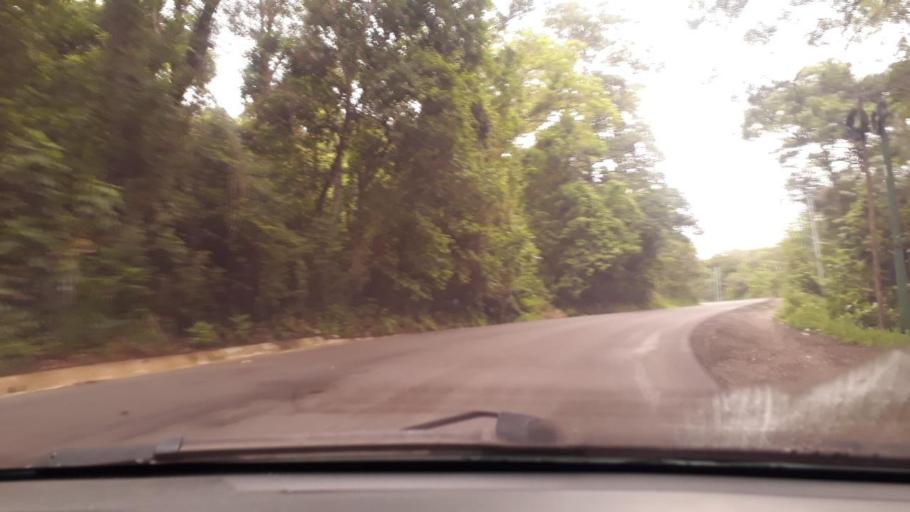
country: GT
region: Chiquimula
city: Concepcion Las Minas
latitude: 14.5589
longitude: -89.4539
